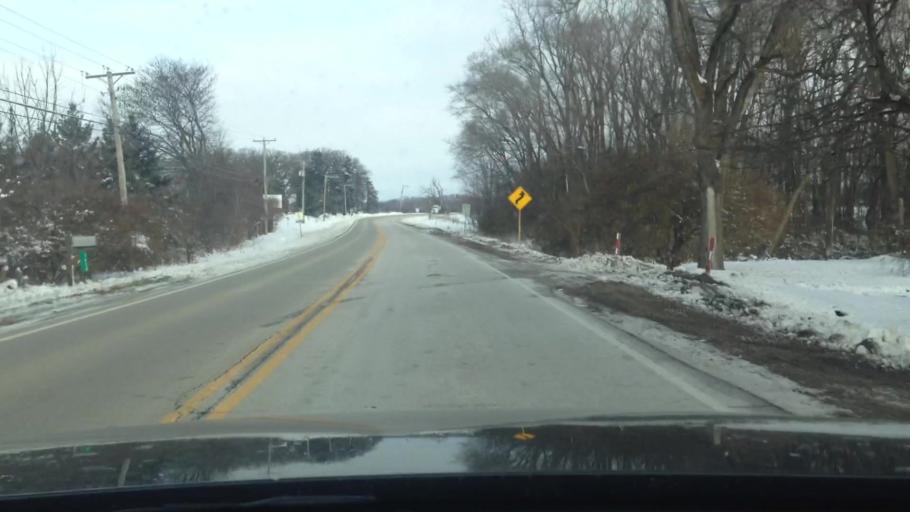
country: US
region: Illinois
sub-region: McHenry County
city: Woodstock
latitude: 42.3468
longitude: -88.4436
